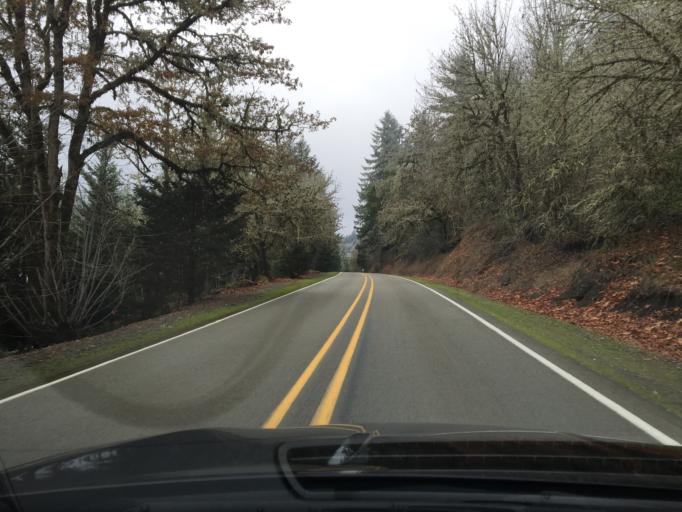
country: US
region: Oregon
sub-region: Douglas County
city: Sutherlin
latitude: 43.3828
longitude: -123.5234
